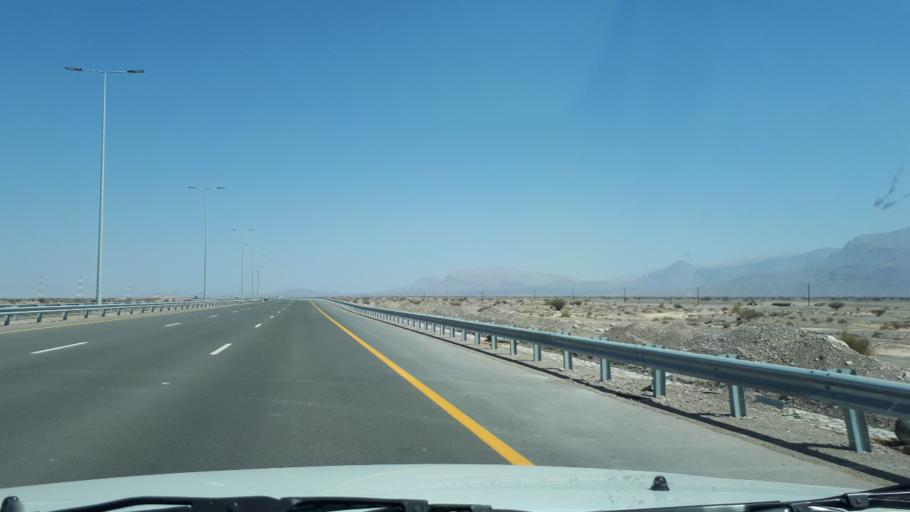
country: OM
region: Ash Sharqiyah
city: Badiyah
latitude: 22.3310
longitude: 59.1300
